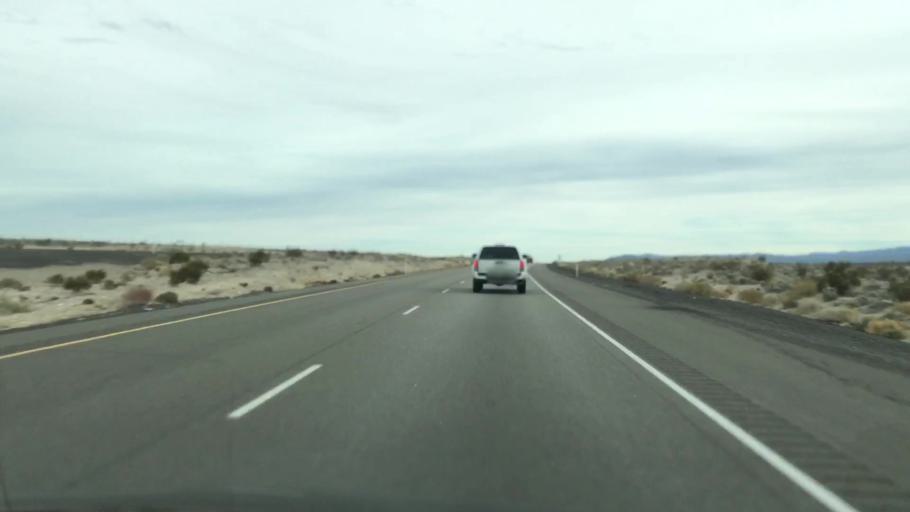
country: US
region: Nevada
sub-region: Nye County
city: Pahrump
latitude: 36.6003
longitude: -115.9642
